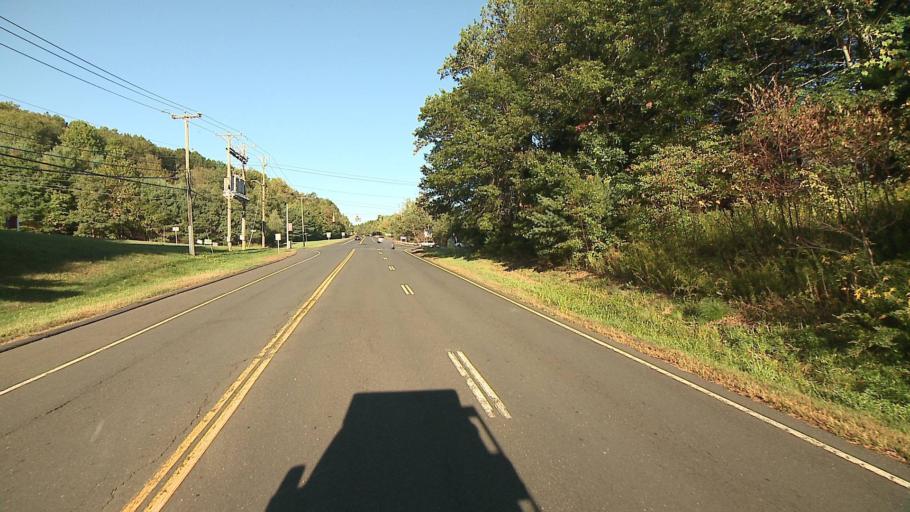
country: US
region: Connecticut
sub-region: Litchfield County
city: New Hartford Center
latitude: 41.8299
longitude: -73.0159
